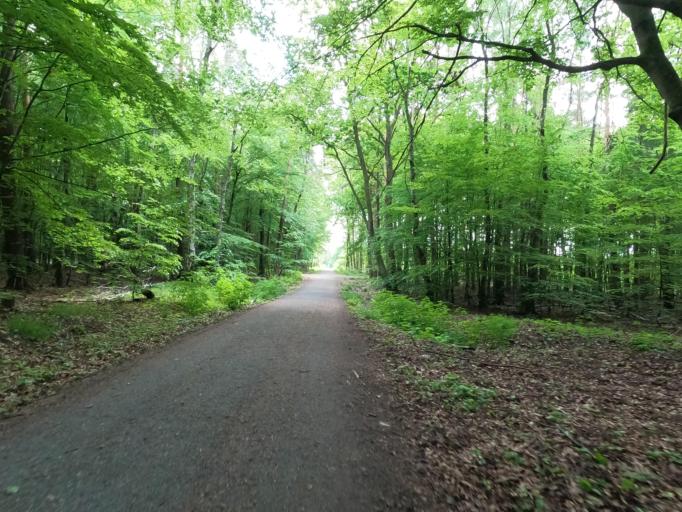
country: DE
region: Hesse
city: Langen
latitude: 50.0039
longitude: 8.6371
